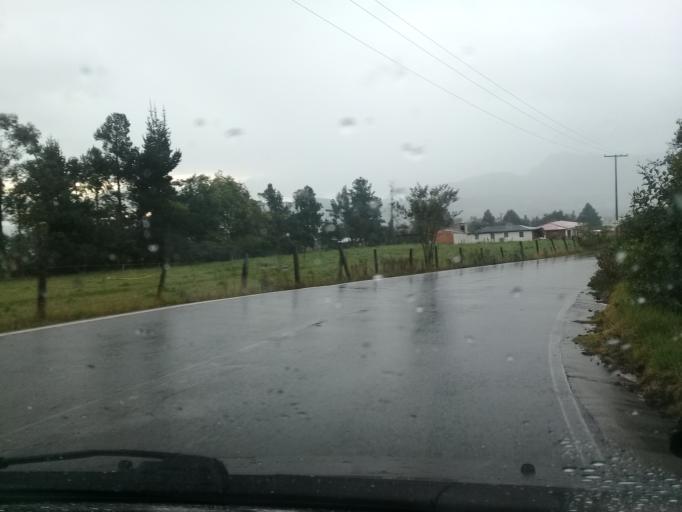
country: CO
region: Cundinamarca
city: Guasca
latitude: 4.8578
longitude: -73.8609
